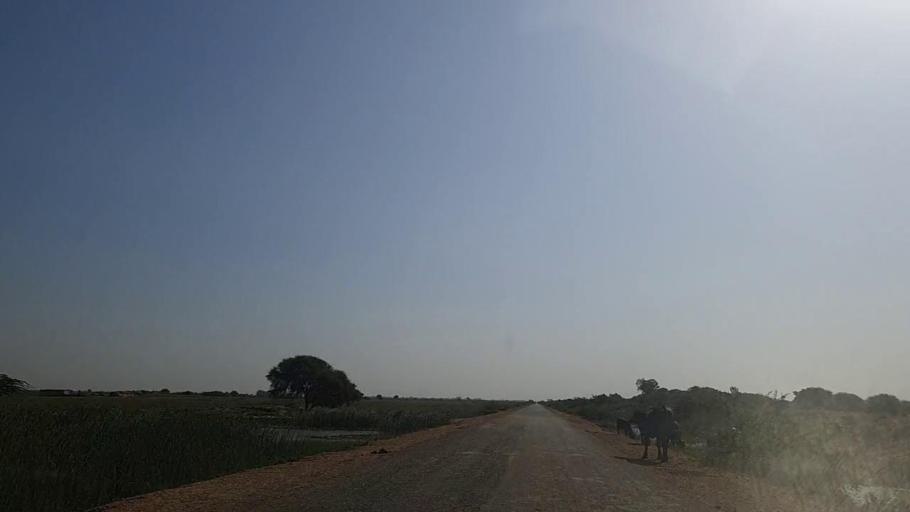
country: PK
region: Sindh
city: Jati
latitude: 24.4520
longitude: 68.2638
